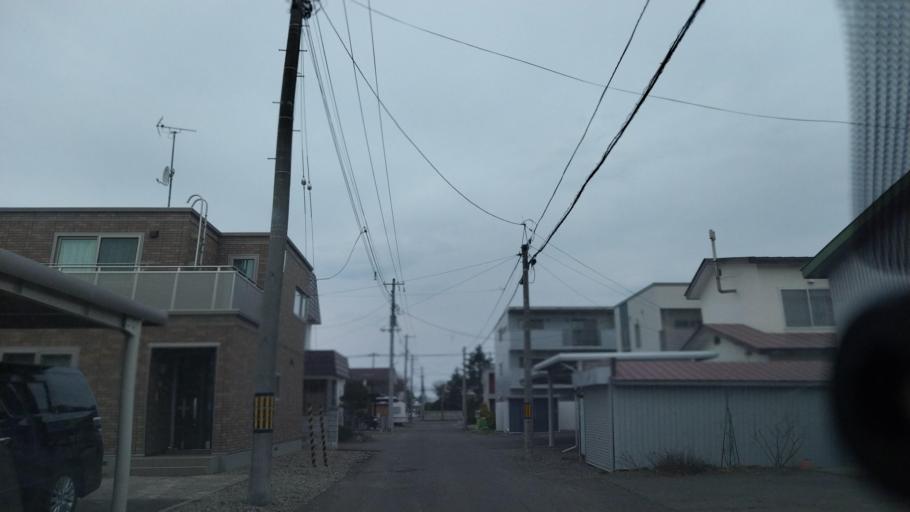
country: JP
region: Hokkaido
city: Obihiro
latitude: 42.9214
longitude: 143.2202
